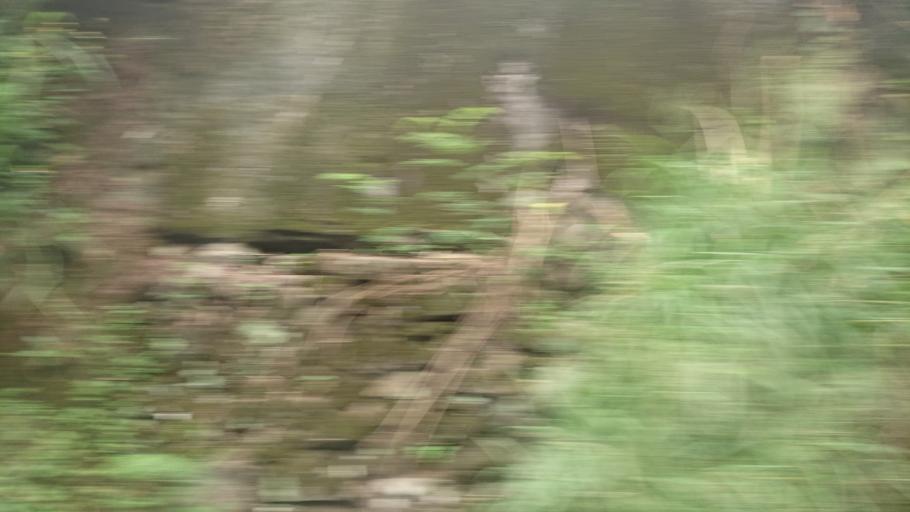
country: TW
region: Taiwan
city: Lugu
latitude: 23.8270
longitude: 120.8586
